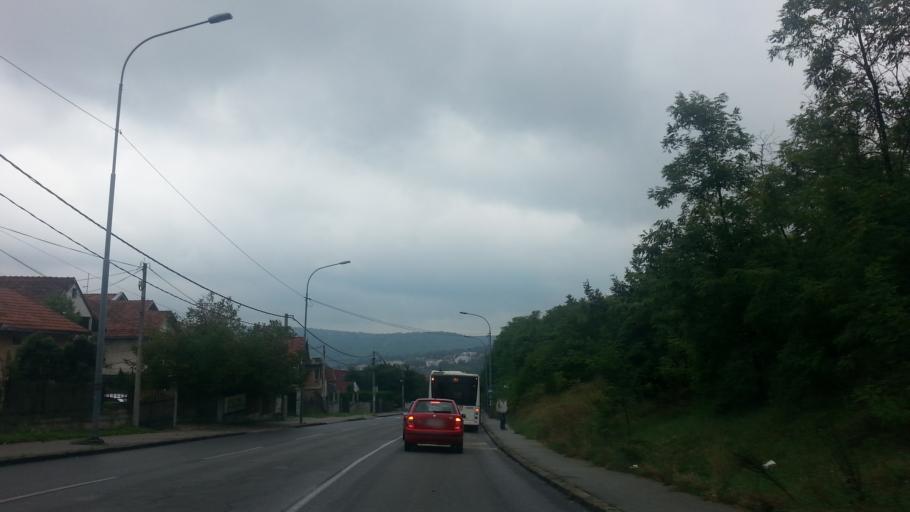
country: RS
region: Central Serbia
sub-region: Belgrade
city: Vozdovac
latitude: 44.7546
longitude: 20.4682
